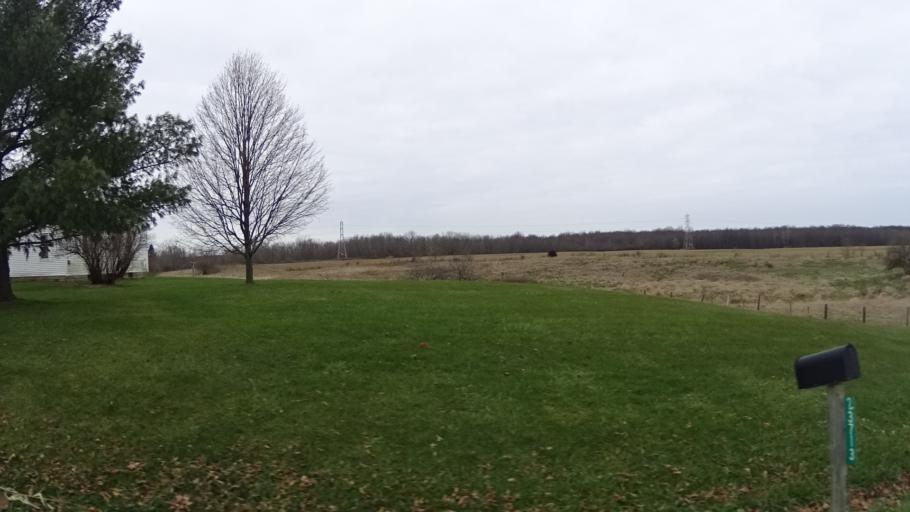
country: US
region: Ohio
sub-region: Lorain County
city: Wellington
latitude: 41.1516
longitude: -82.2691
